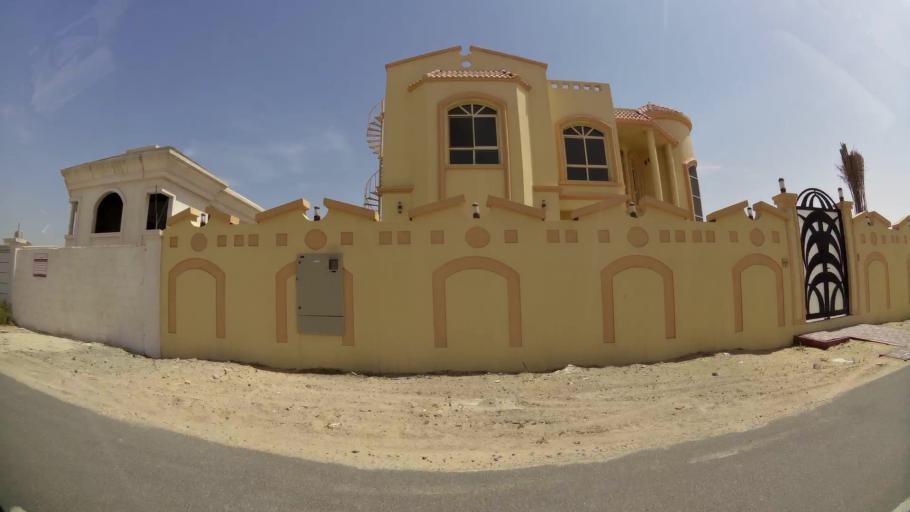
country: AE
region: Ash Shariqah
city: Sharjah
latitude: 25.1796
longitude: 55.4251
